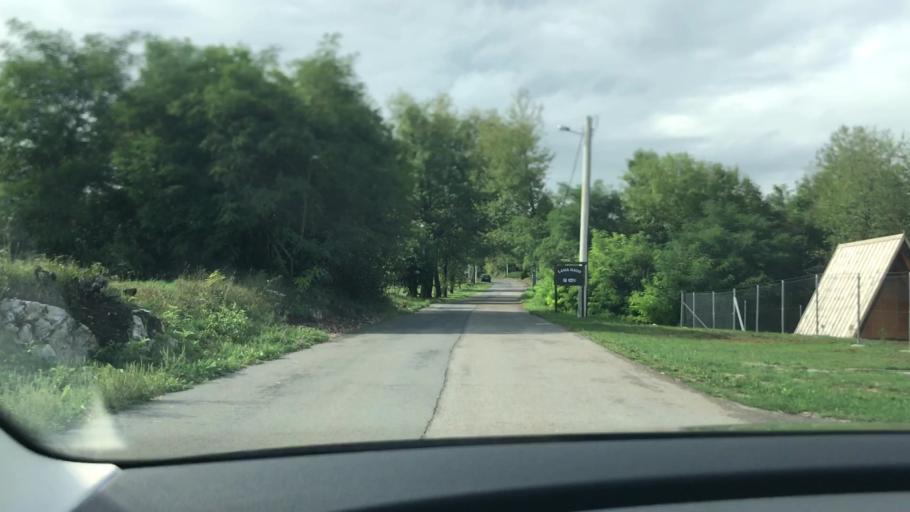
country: BA
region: Federation of Bosnia and Herzegovina
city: Izacic
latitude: 44.8761
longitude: 15.7159
